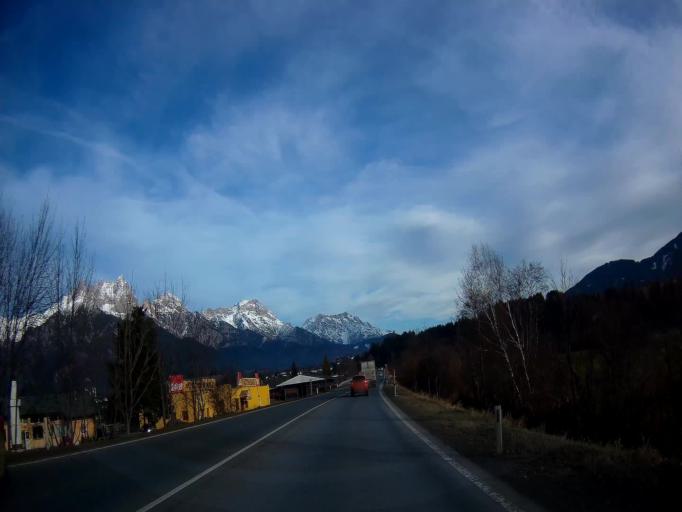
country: AT
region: Salzburg
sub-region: Politischer Bezirk Zell am See
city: Saalfelden am Steinernen Meer
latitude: 47.4190
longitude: 12.8234
